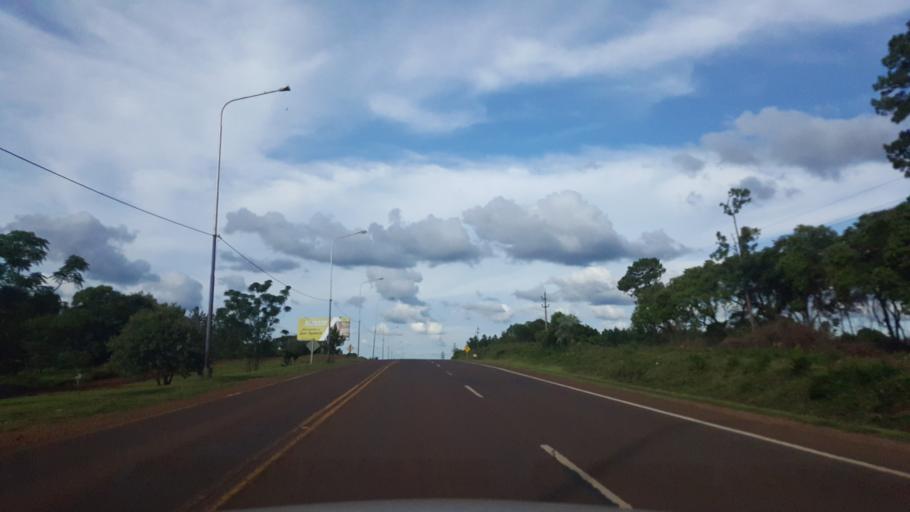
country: AR
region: Misiones
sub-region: Departamento de San Ignacio
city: San Ignacio
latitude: -27.2592
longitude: -55.5296
